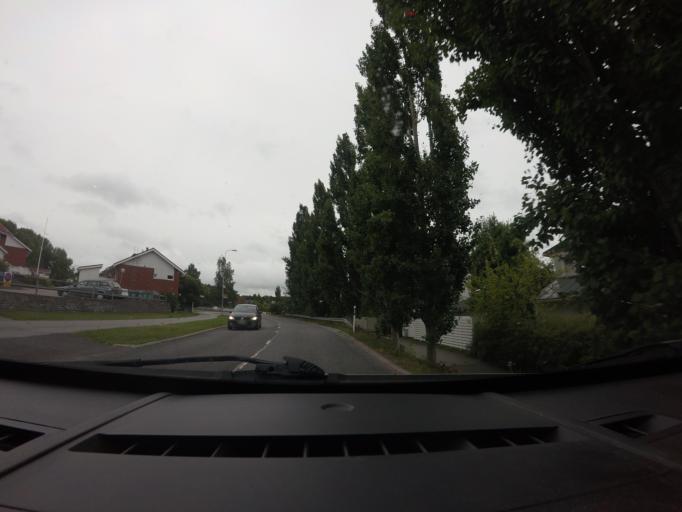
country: FI
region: Varsinais-Suomi
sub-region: Turku
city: Turku
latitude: 60.4123
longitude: 22.2913
